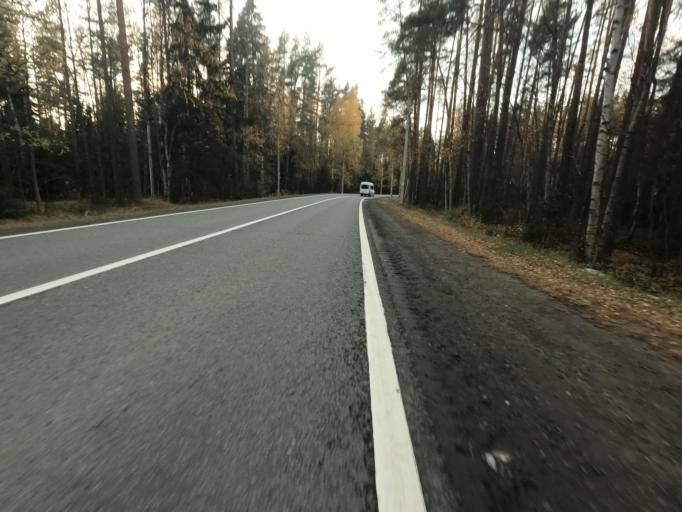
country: RU
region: St.-Petersburg
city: Repino
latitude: 60.1914
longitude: 29.8592
